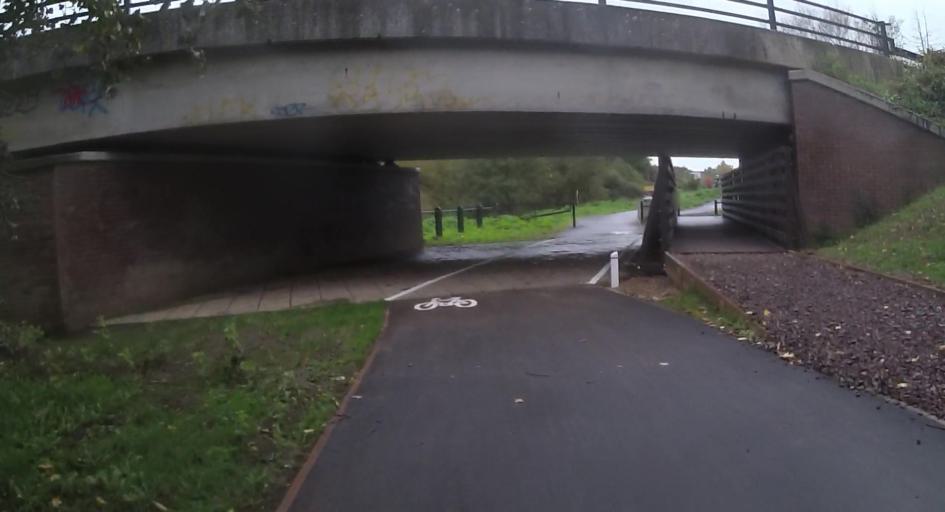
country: GB
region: England
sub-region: Surrey
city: Byfleet
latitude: 51.3484
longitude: -0.4677
